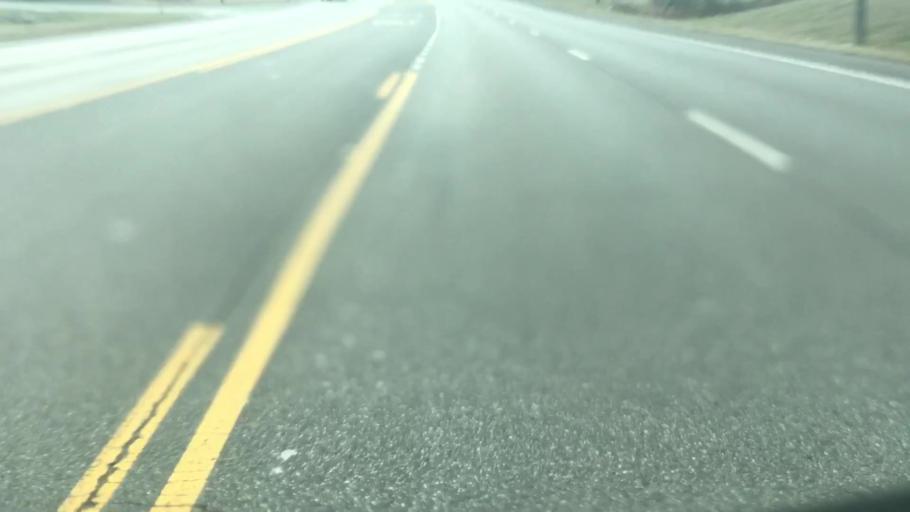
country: US
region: Alabama
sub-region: Walker County
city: Jasper
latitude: 33.8193
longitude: -87.2338
